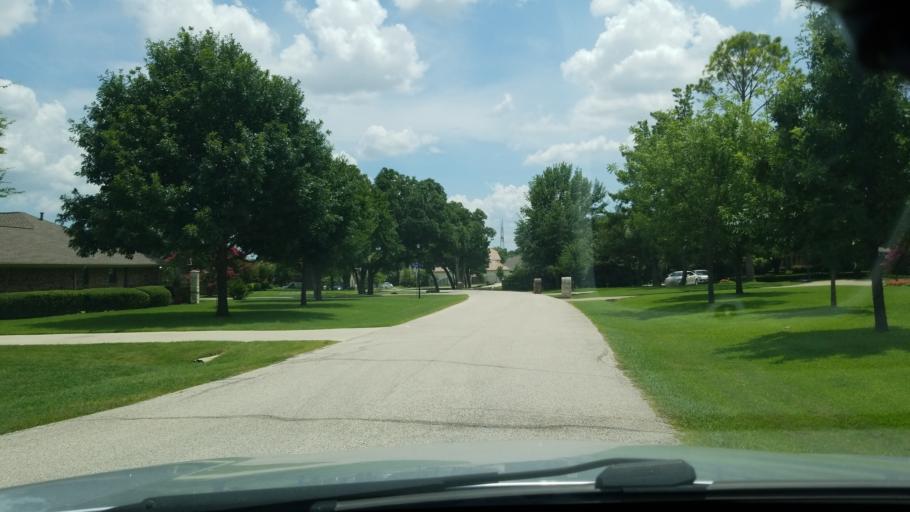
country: US
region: Texas
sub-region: Dallas County
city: Coppell
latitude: 32.9587
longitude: -96.9806
